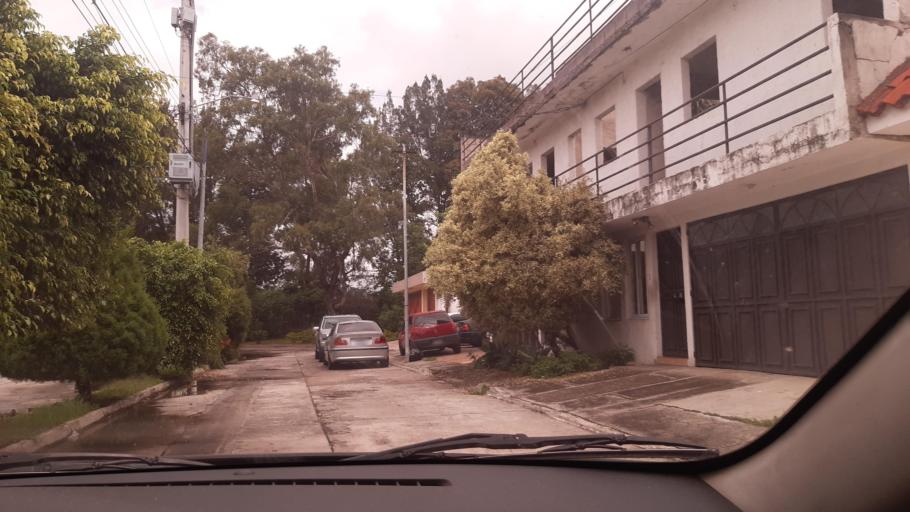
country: GT
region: Guatemala
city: Petapa
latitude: 14.5057
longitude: -90.5462
